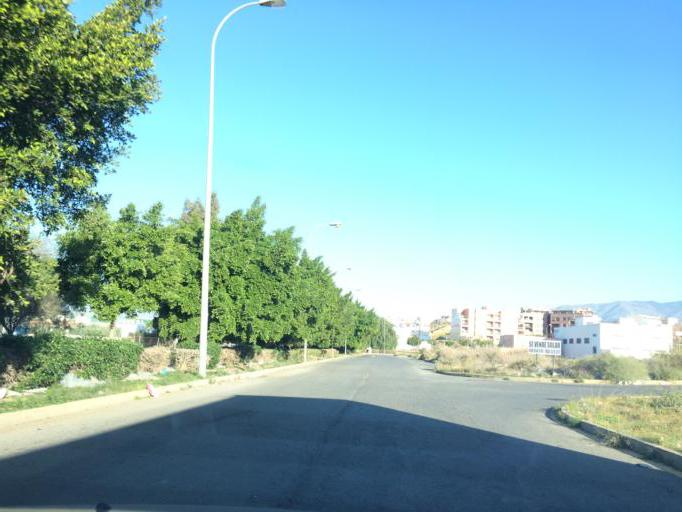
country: ES
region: Andalusia
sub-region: Provincia de Almeria
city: Viator
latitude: 36.8804
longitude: -2.4235
